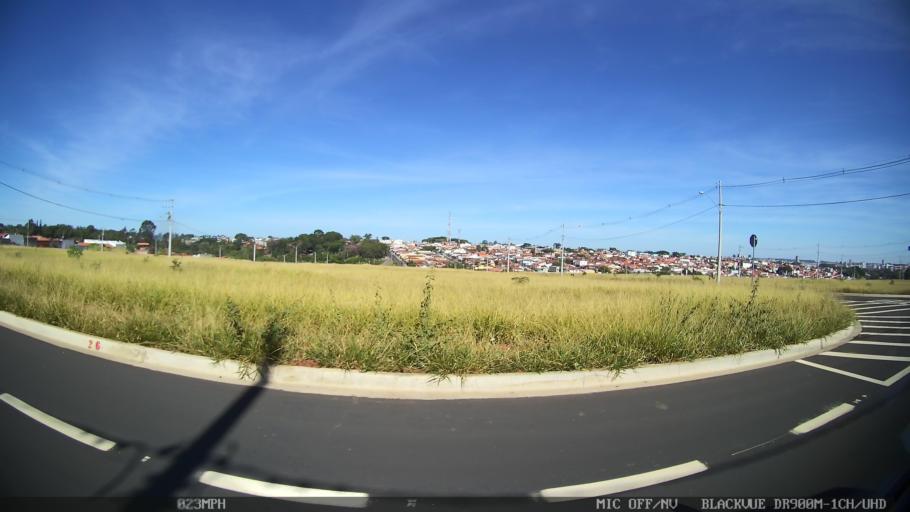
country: BR
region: Sao Paulo
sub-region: Franca
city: Franca
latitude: -20.5536
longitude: -47.3662
